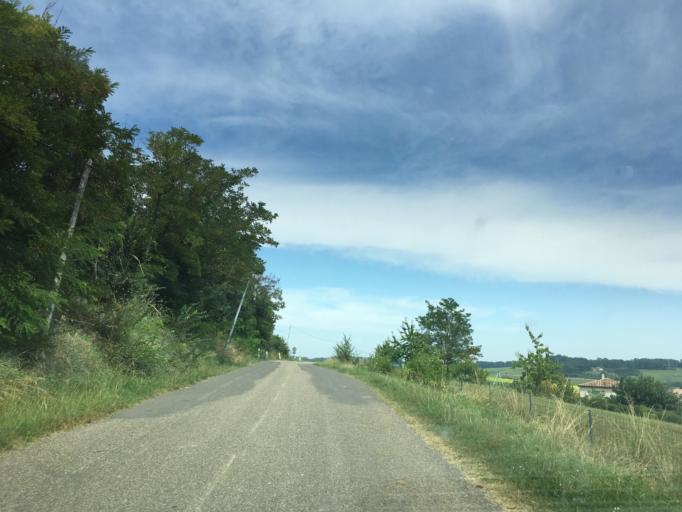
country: FR
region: Midi-Pyrenees
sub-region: Departement du Tarn-et-Garonne
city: Auvillar
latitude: 44.0377
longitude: 0.8417
